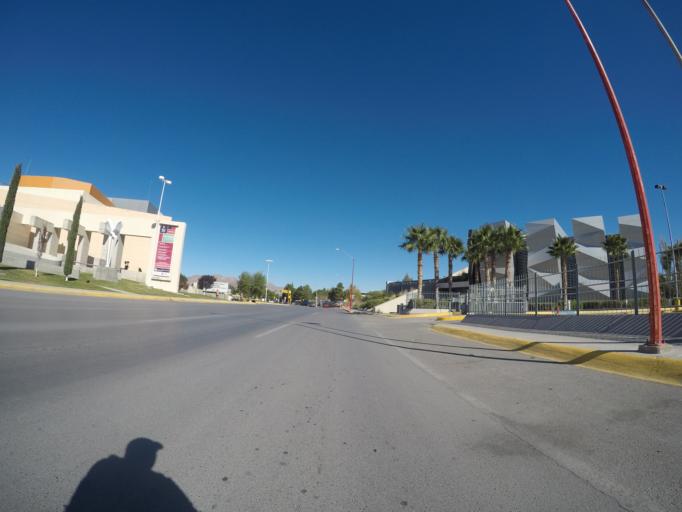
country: MX
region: Chihuahua
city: Ciudad Juarez
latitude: 31.7432
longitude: -106.4439
